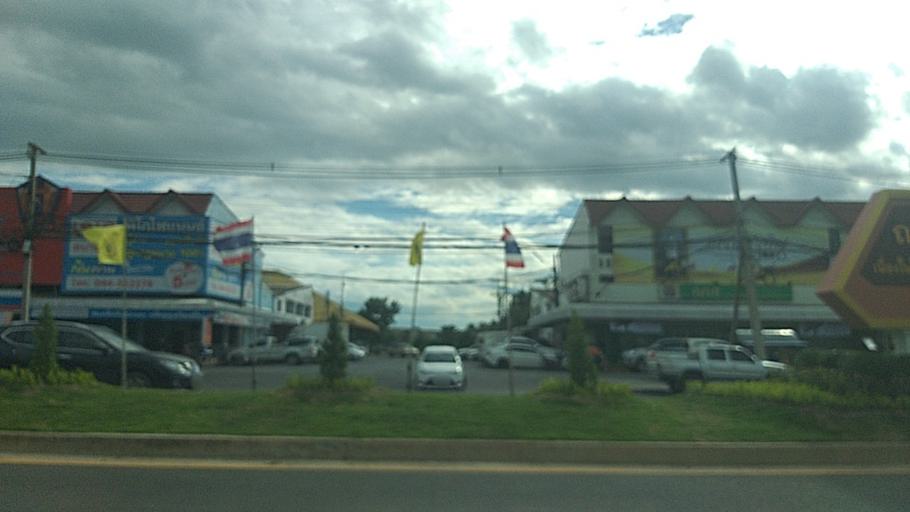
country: TH
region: Surin
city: Prasat
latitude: 14.6294
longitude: 103.4091
